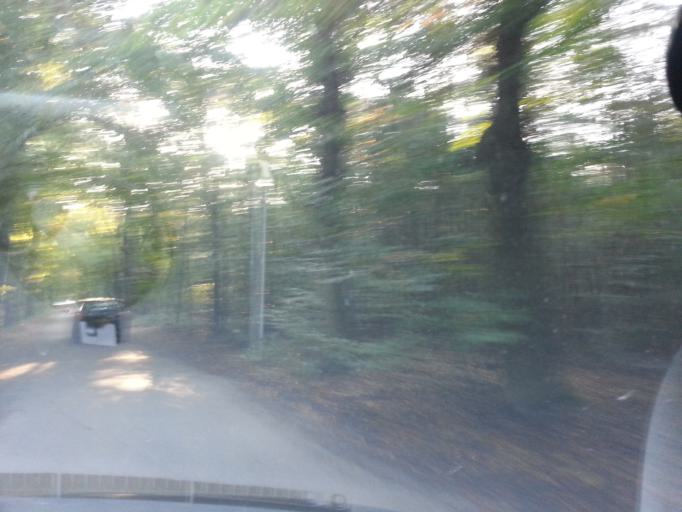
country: NL
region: Utrecht
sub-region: Gemeente Utrechtse Heuvelrug
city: Driebergen-Rijsenburg
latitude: 52.0984
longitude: 5.2777
